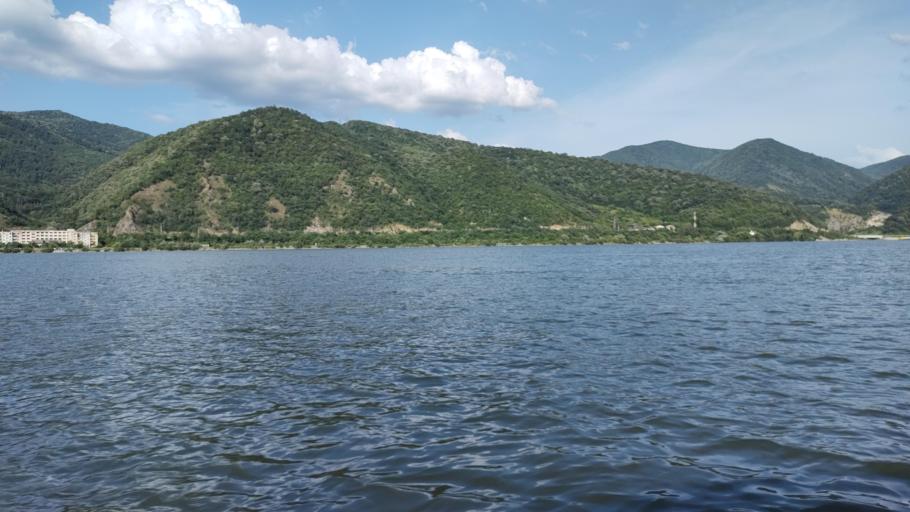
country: RO
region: Caras-Severin
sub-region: Comuna Berzasca
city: Berzasca
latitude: 44.6263
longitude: 21.9955
